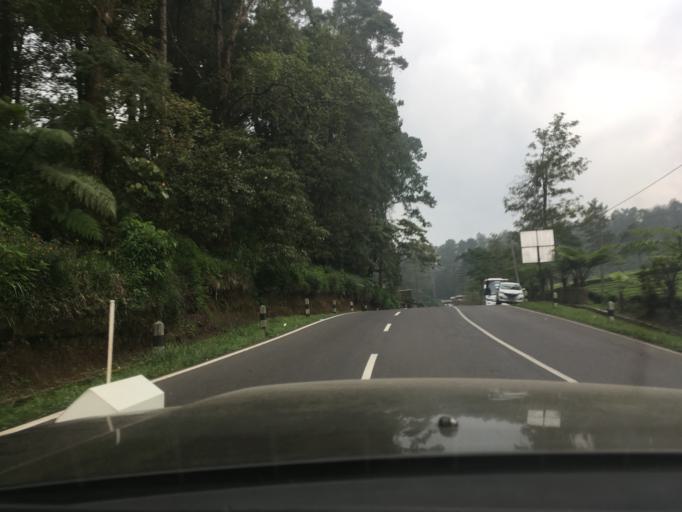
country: ID
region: West Java
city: Lembang
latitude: -6.7713
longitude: 107.6376
